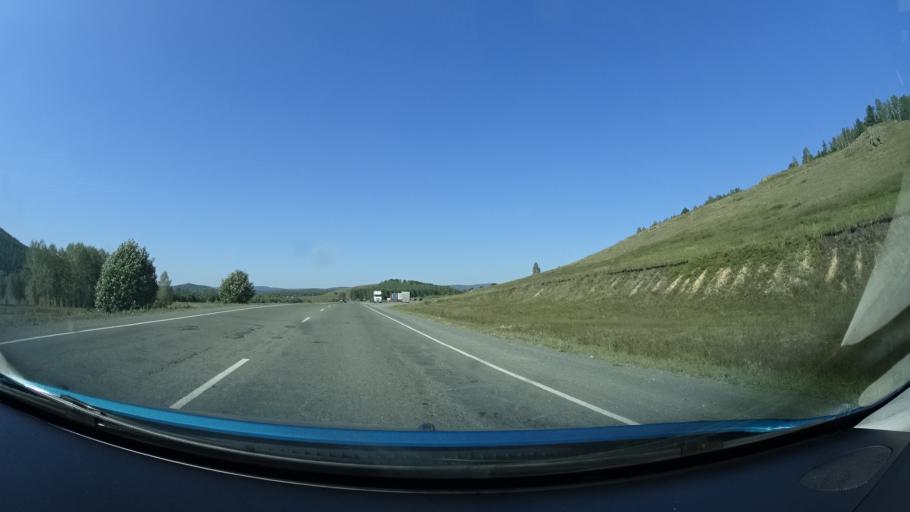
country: RU
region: Bashkortostan
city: Abzakovo
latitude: 53.8227
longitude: 58.6235
